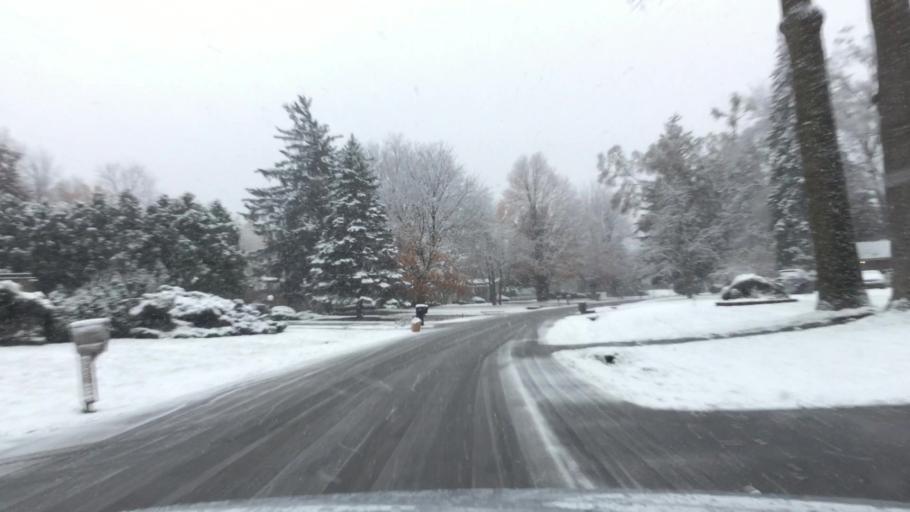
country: US
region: Michigan
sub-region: Oakland County
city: Southfield
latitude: 42.4676
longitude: -83.2287
